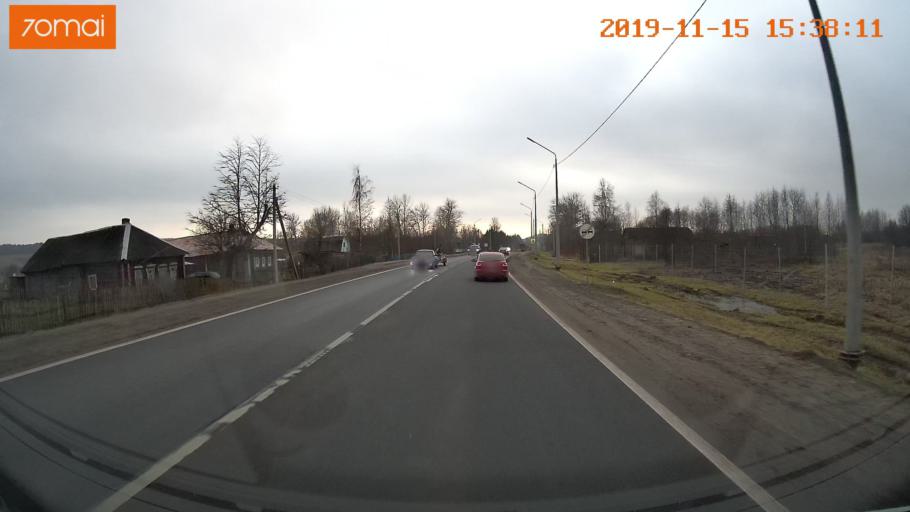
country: RU
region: Jaroslavl
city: Danilov
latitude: 58.0320
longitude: 40.0829
